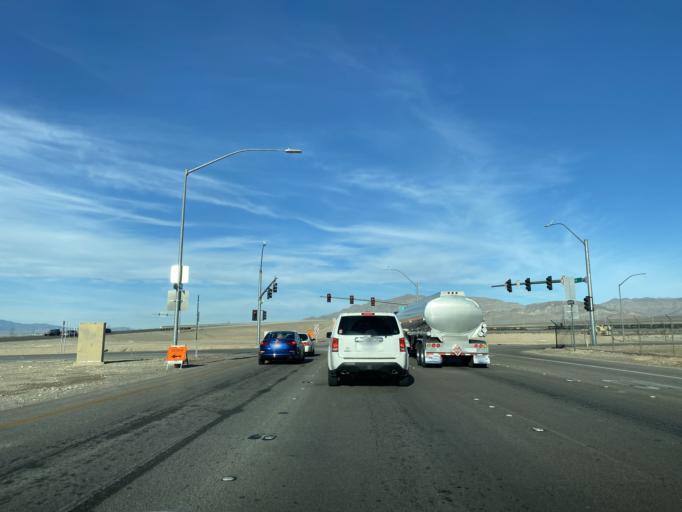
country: US
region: Nevada
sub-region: Clark County
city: Nellis Air Force Base
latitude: 36.2768
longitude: -115.0597
